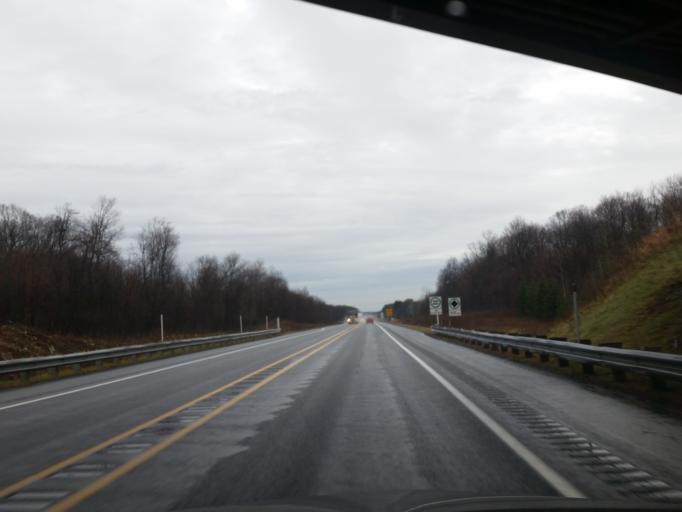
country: CA
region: Quebec
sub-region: Laurentides
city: Saint-Colomban
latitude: 45.6823
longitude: -74.1335
